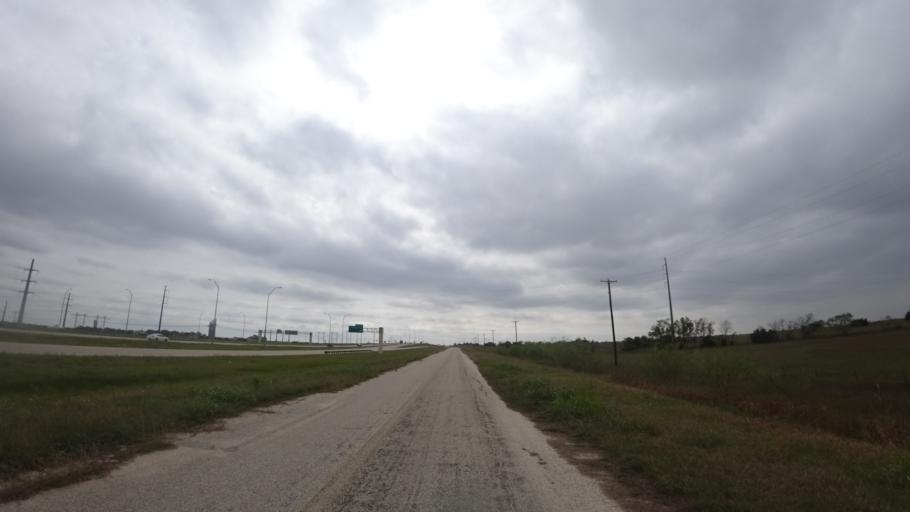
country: US
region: Texas
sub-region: Travis County
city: Pflugerville
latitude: 30.4110
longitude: -97.5856
